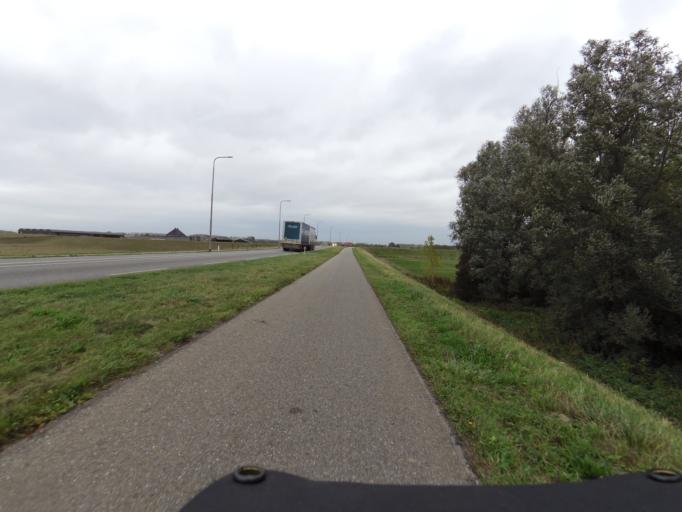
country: NL
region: Gelderland
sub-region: Gemeente Zevenaar
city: Zevenaar
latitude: 51.8958
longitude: 6.1051
